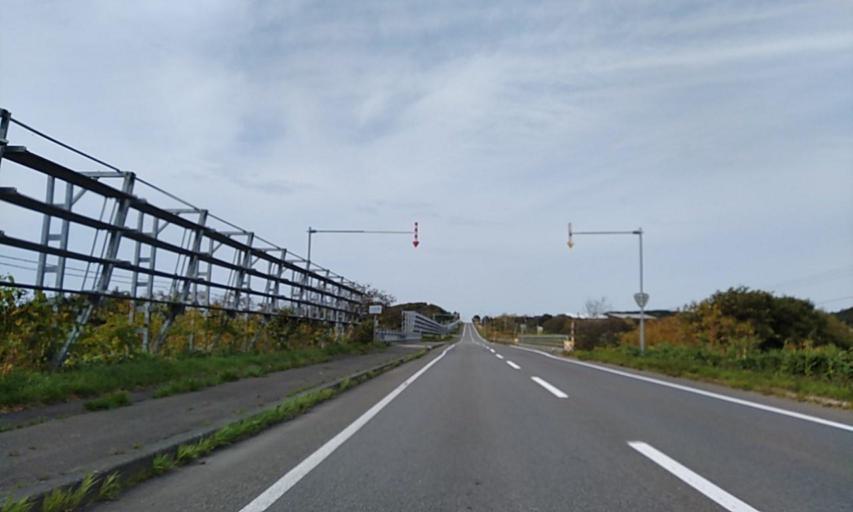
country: JP
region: Hokkaido
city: Makubetsu
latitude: 44.7731
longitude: 141.7921
